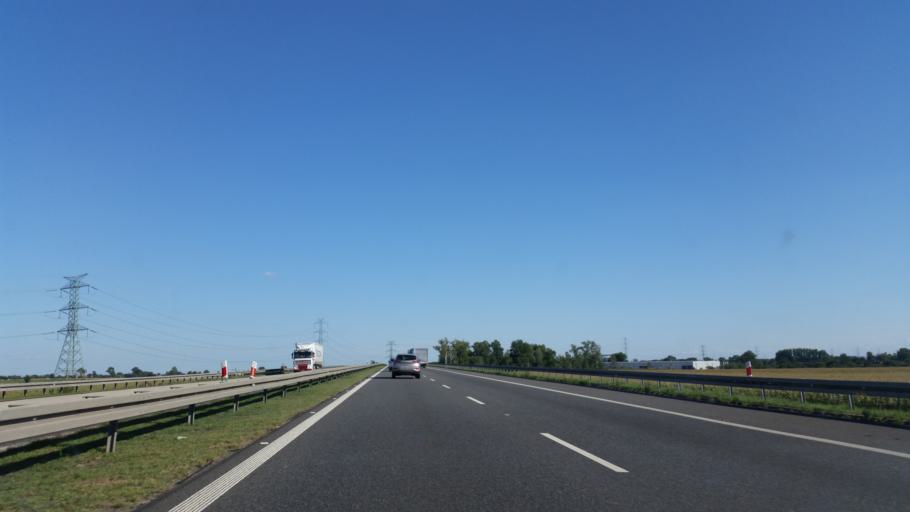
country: PL
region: Lower Silesian Voivodeship
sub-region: Powiat wroclawski
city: Zorawina
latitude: 50.9948
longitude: 17.0473
